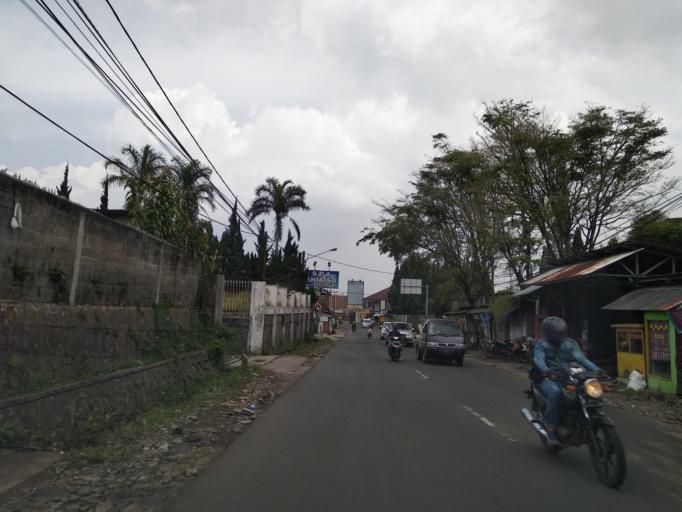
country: ID
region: West Java
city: Lembang
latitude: -6.8208
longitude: 107.6104
